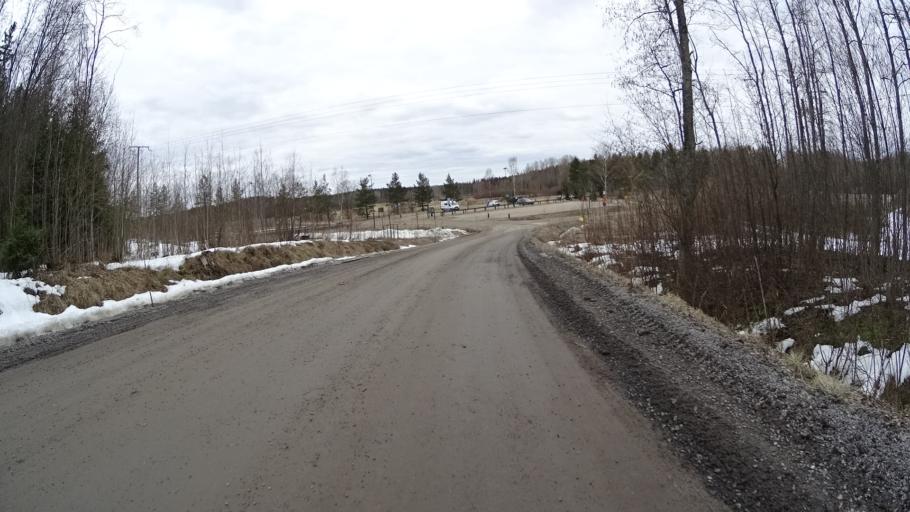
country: FI
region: Uusimaa
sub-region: Helsinki
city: Kilo
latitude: 60.2873
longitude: 24.8188
